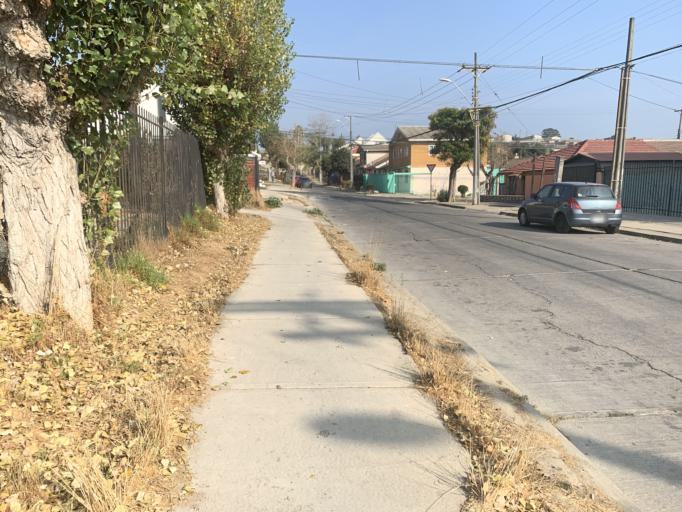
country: CL
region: Valparaiso
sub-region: Provincia de Marga Marga
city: Quilpue
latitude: -33.0501
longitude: -71.4345
